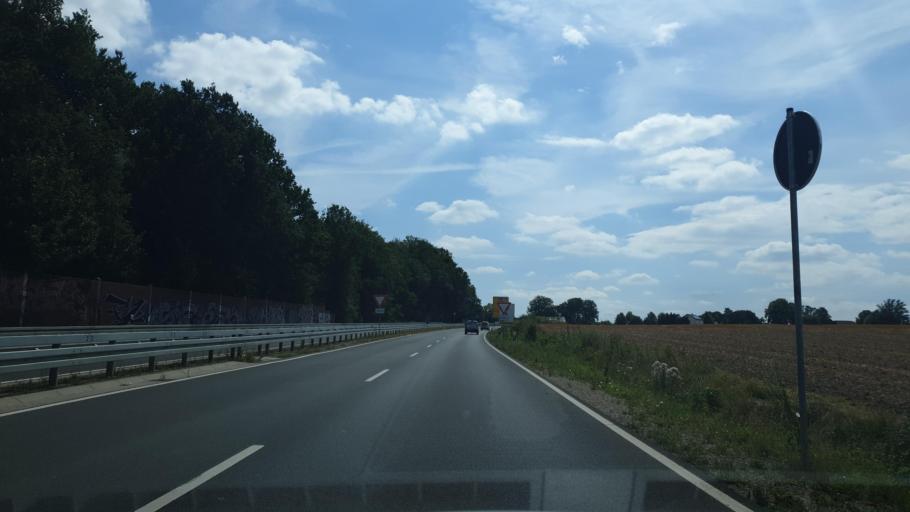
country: DE
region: North Rhine-Westphalia
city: Loehne
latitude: 52.1803
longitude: 8.7492
